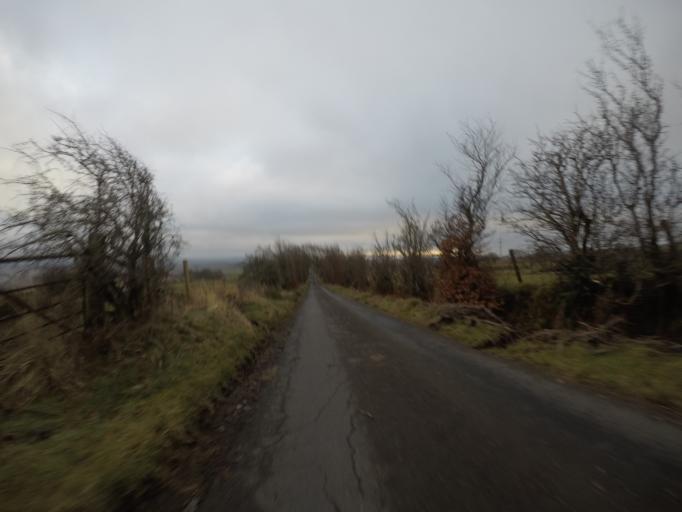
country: GB
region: Scotland
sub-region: North Ayrshire
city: Dalry
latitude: 55.7247
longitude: -4.7633
